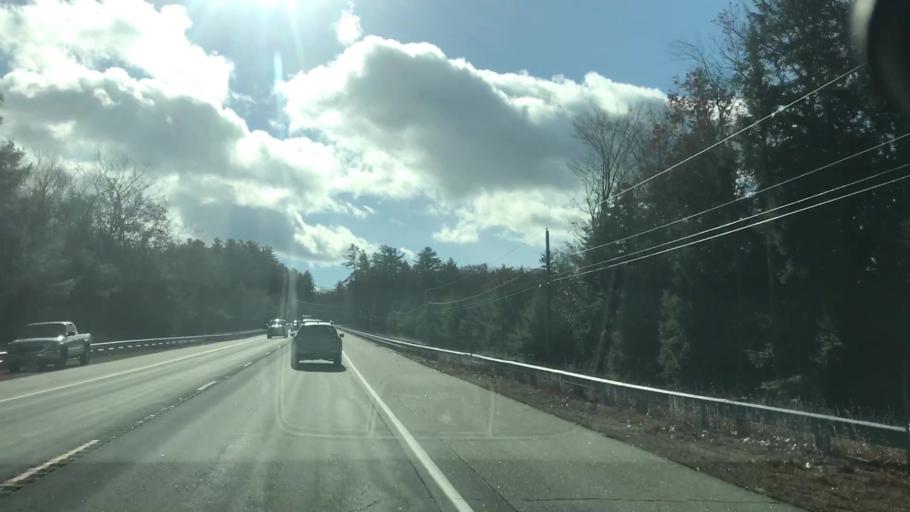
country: US
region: New Hampshire
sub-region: Carroll County
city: Wolfeboro
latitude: 43.5285
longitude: -71.2045
